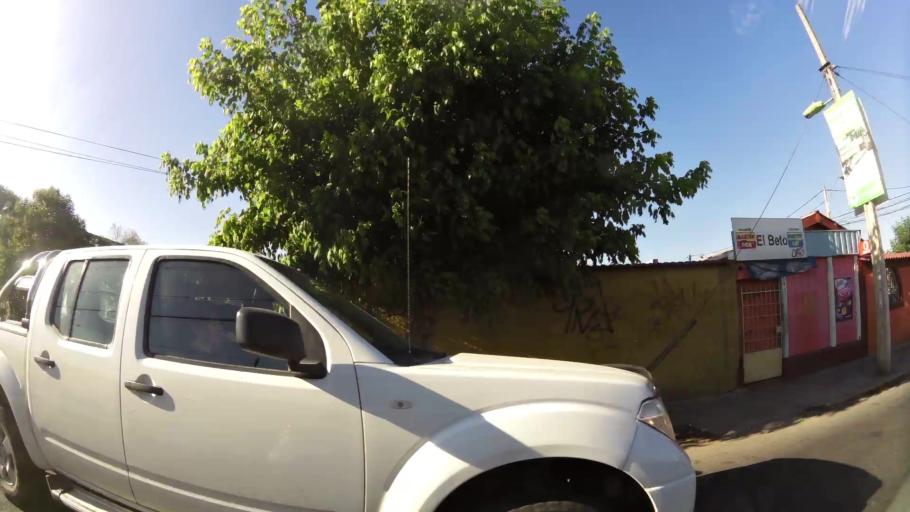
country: CL
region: Santiago Metropolitan
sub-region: Provincia de Maipo
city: San Bernardo
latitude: -33.5479
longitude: -70.6782
